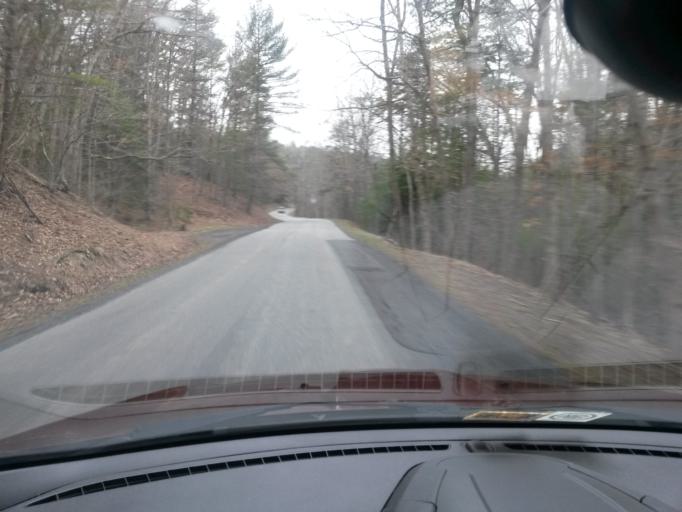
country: US
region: Virginia
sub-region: Bath County
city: Warm Springs
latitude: 38.0307
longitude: -79.8587
